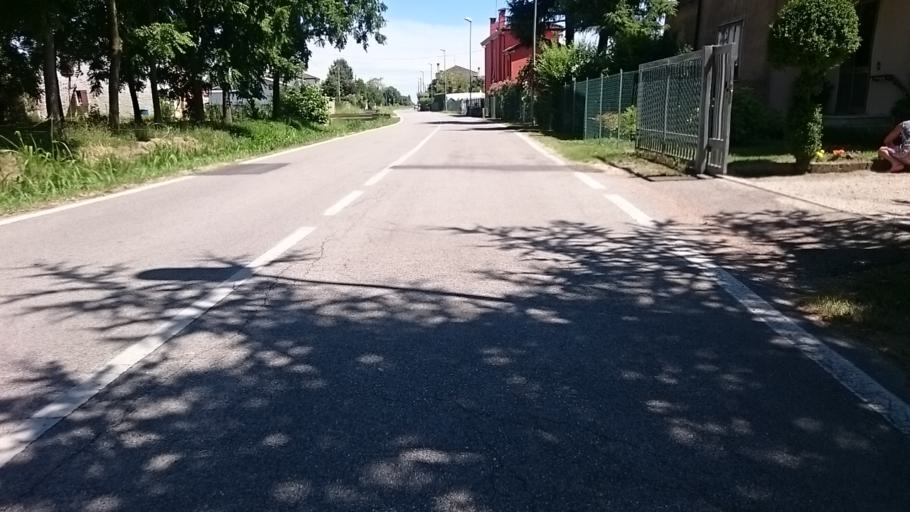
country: IT
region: Veneto
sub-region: Provincia di Padova
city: Pionca
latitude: 45.4687
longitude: 11.9797
